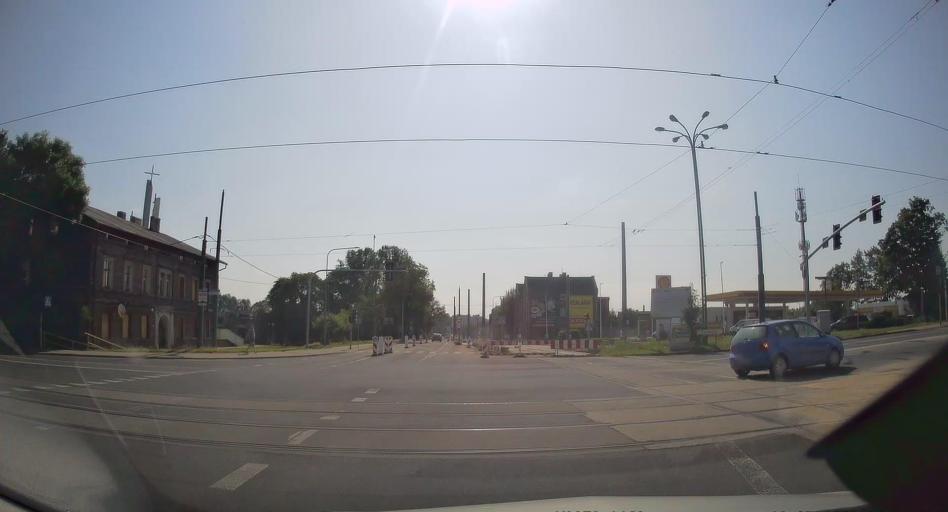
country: PL
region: Silesian Voivodeship
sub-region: Swietochlowice
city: Swietochlowice
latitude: 50.3051
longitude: 18.9192
